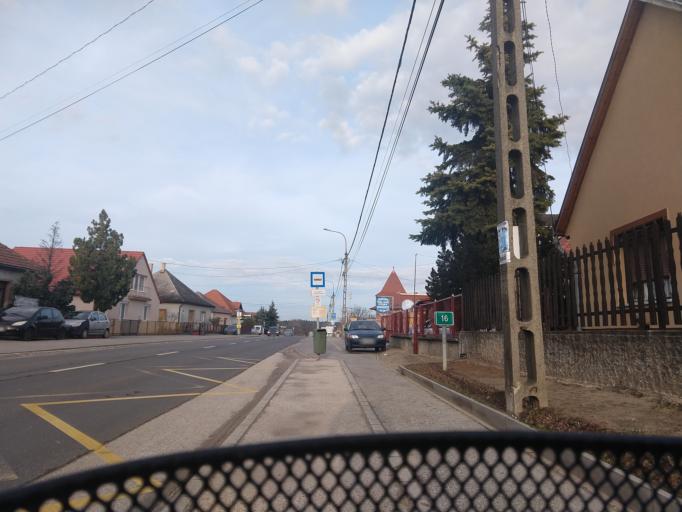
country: HU
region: Pest
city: Orbottyan
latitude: 47.6656
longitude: 19.2769
